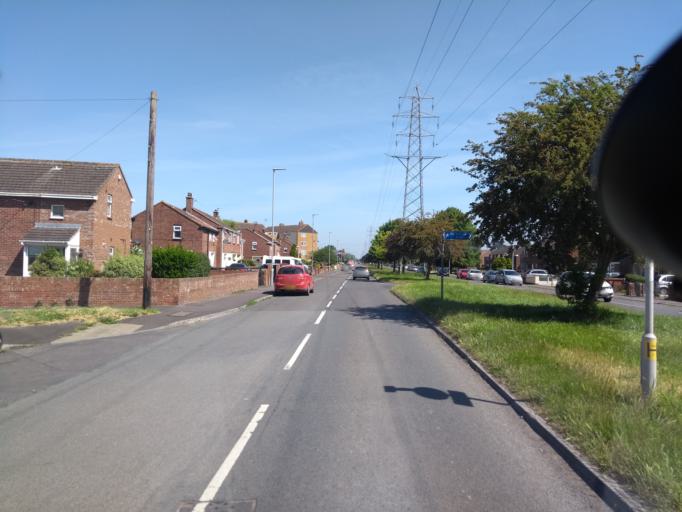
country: GB
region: England
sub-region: Somerset
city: Bridgwater
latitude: 51.1256
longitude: -2.9829
